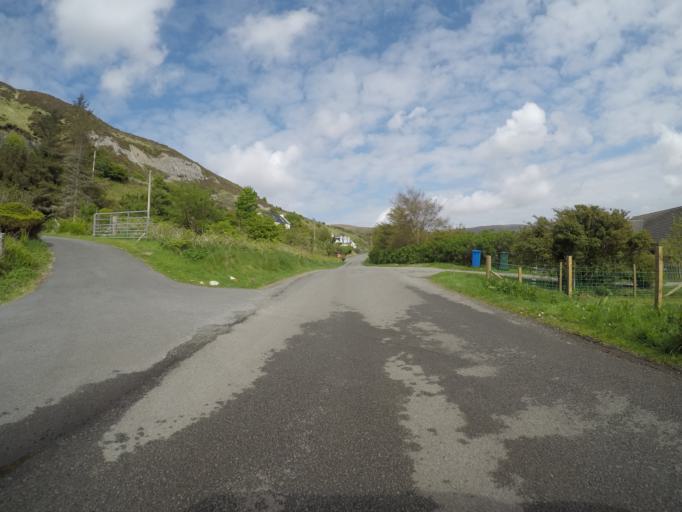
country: GB
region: Scotland
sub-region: Highland
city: Portree
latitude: 57.5898
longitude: -6.3790
